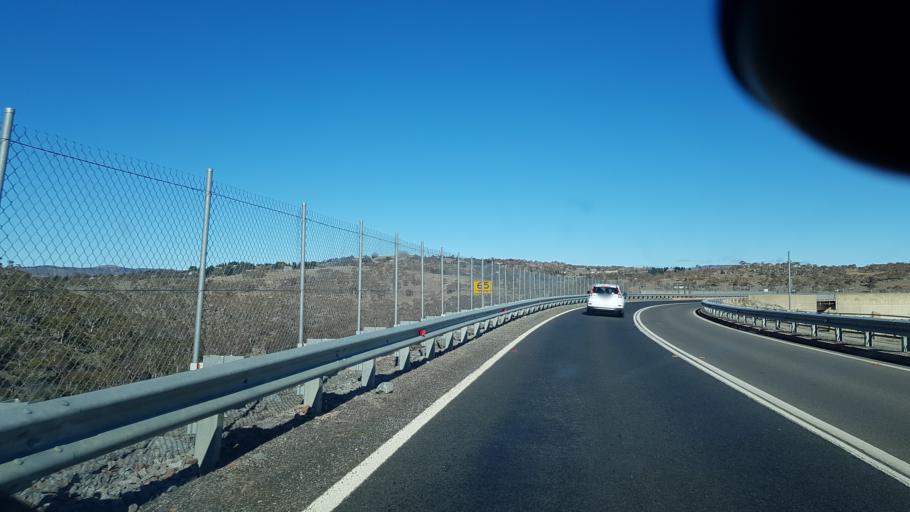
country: AU
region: New South Wales
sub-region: Snowy River
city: Jindabyne
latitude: -36.4336
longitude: 148.6329
